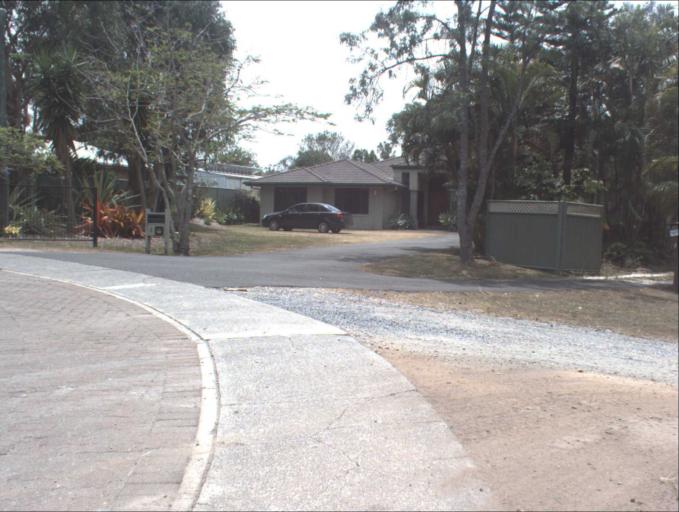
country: AU
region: Queensland
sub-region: Logan
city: Slacks Creek
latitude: -27.6676
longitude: 153.1858
